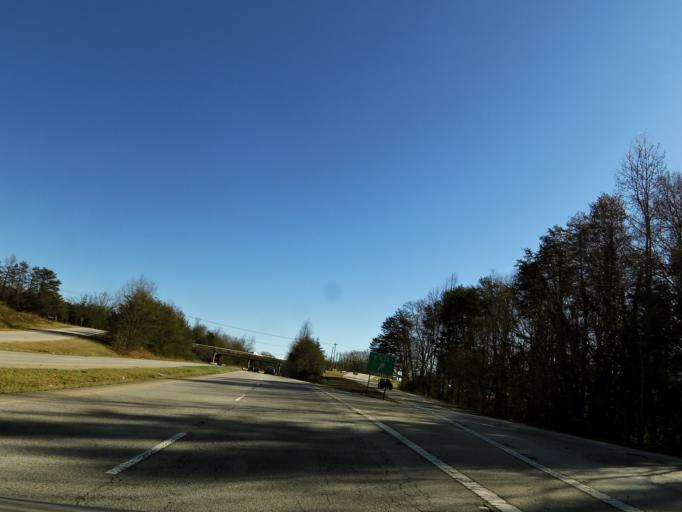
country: US
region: South Carolina
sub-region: Greenville County
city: Sans Souci
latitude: 34.9160
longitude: -82.4310
